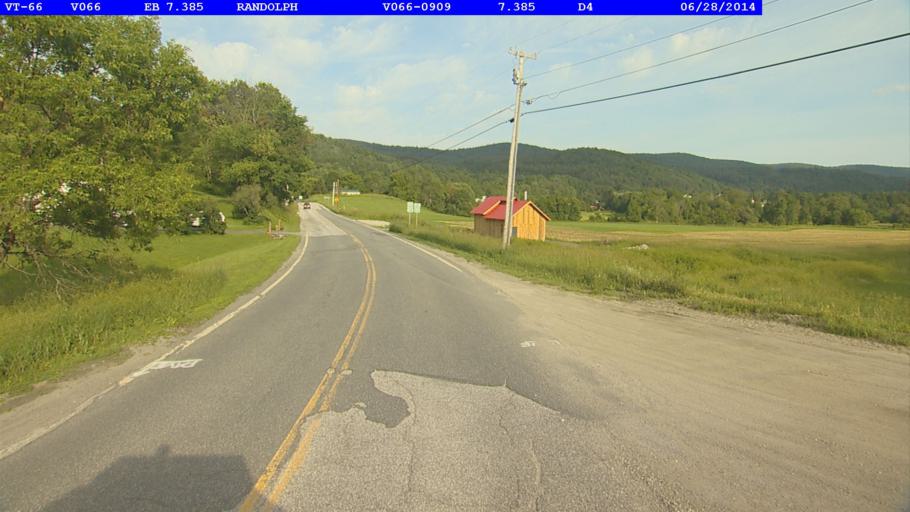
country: US
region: Vermont
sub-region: Orange County
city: Randolph
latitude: 43.9410
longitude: -72.5586
